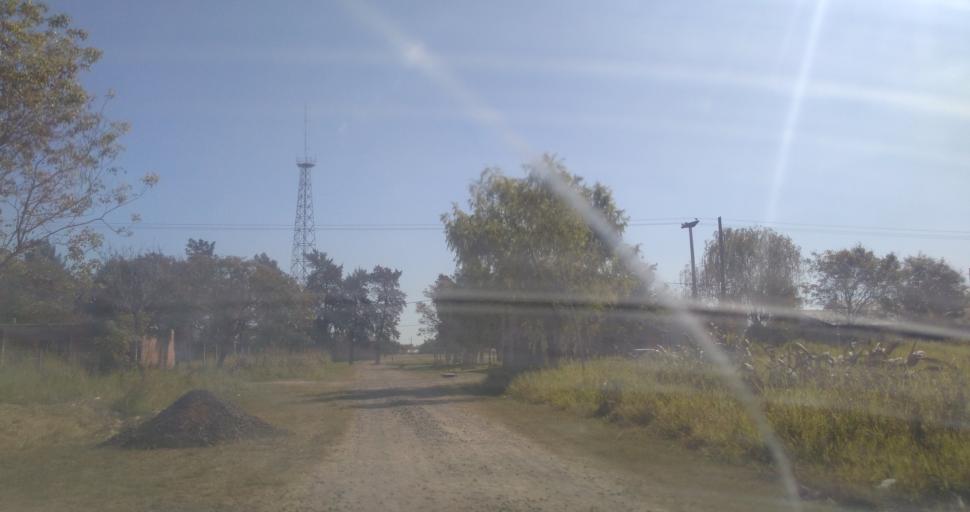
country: AR
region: Chaco
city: Fontana
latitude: -27.4415
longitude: -59.0236
